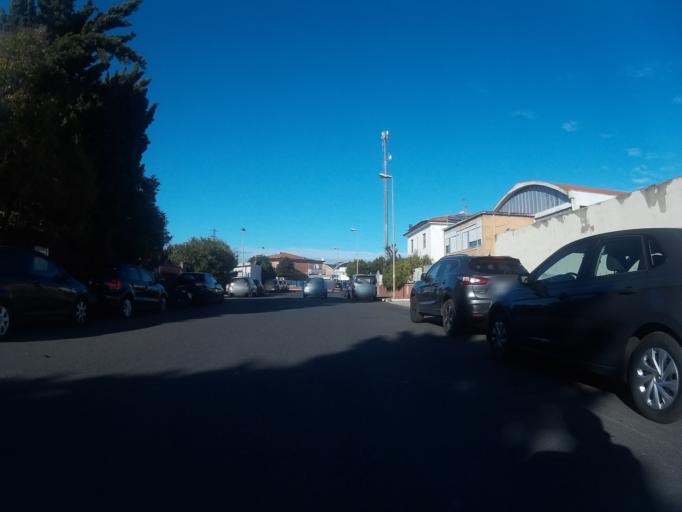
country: IT
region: Tuscany
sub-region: Provincia di Livorno
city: Livorno
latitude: 43.5676
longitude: 10.3370
